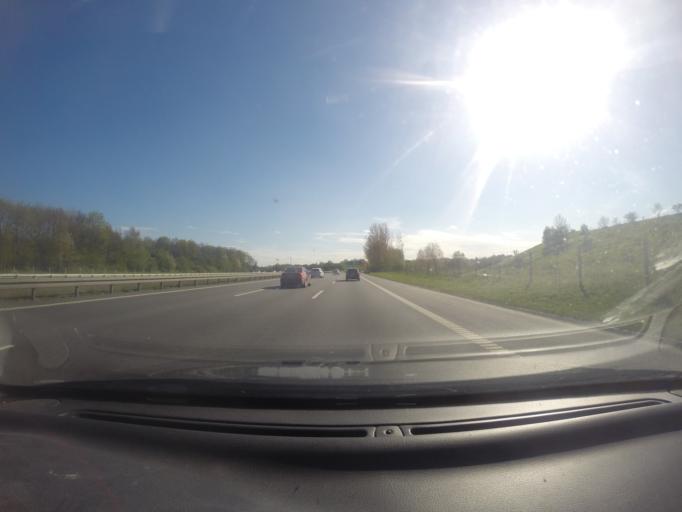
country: DK
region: Capital Region
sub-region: Hoje-Taastrup Kommune
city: Taastrup
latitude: 55.6741
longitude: 12.3224
